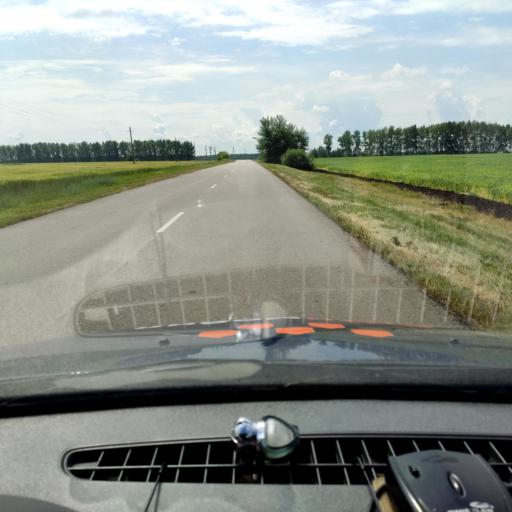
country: RU
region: Voronezj
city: Ramon'
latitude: 52.0188
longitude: 39.3345
